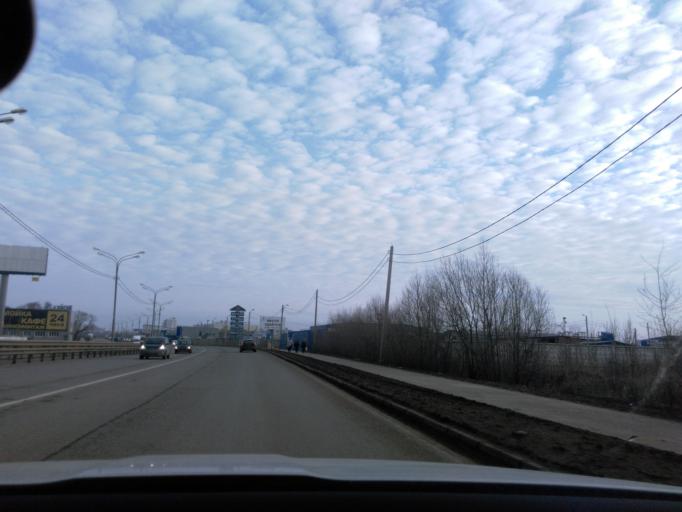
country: RU
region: Moscow
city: Businovo
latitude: 55.9140
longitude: 37.4952
